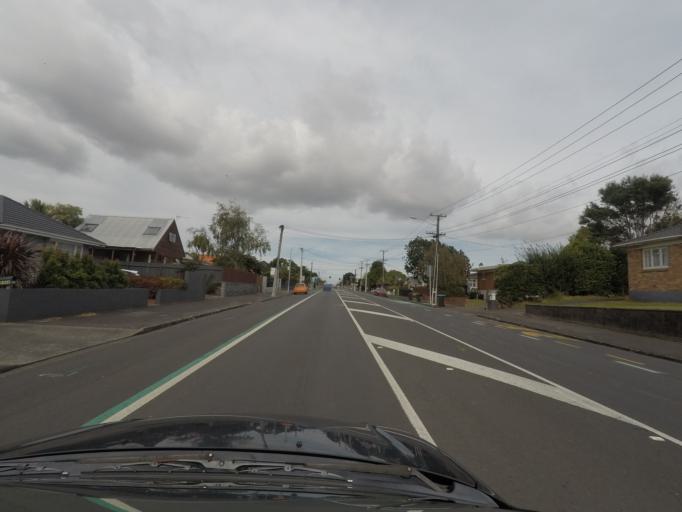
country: NZ
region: Auckland
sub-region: Auckland
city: Auckland
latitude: -36.8831
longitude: 174.7391
